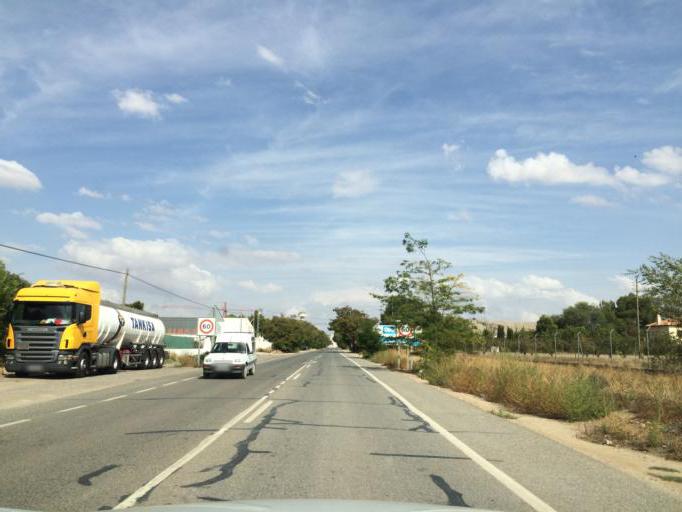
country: ES
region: Castille-La Mancha
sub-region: Provincia de Albacete
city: Albacete
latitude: 38.9972
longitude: -1.8880
